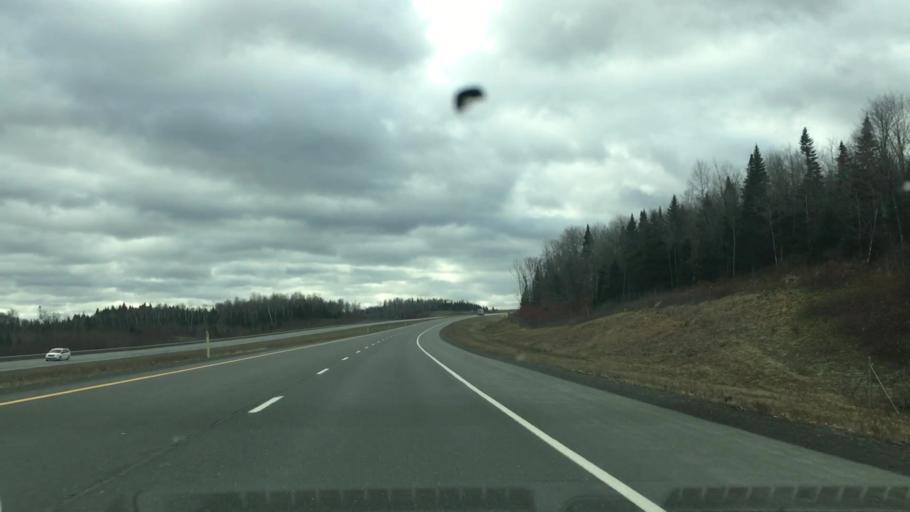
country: US
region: Maine
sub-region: Aroostook County
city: Fort Fairfield
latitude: 46.6674
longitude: -67.7298
